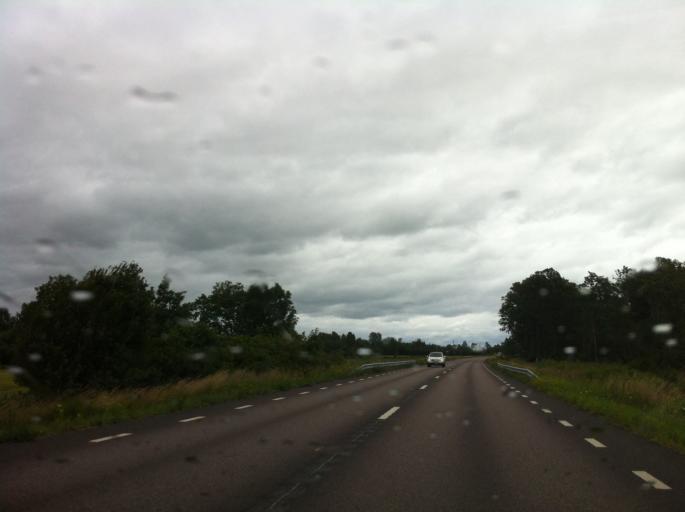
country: SE
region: Kalmar
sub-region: Borgholms Kommun
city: Borgholm
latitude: 57.1049
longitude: 16.9398
